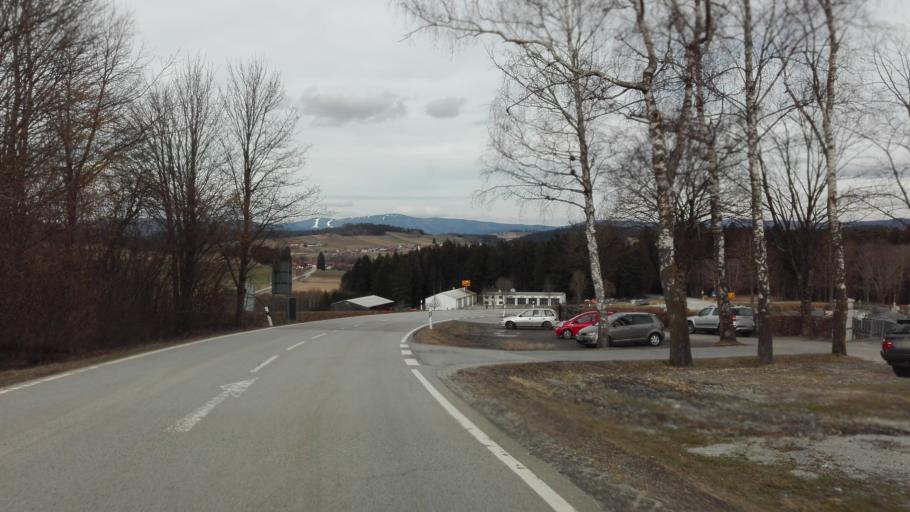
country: DE
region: Bavaria
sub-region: Lower Bavaria
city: Wegscheid
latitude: 48.6032
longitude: 13.7957
